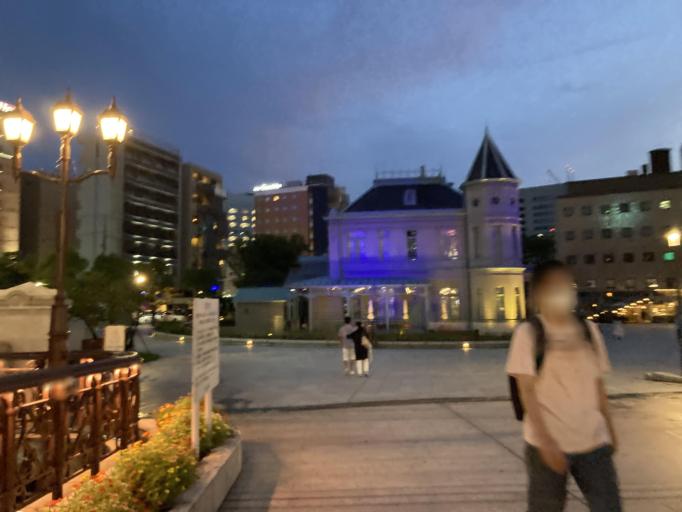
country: JP
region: Fukuoka
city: Fukuoka-shi
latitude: 33.5920
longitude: 130.4049
